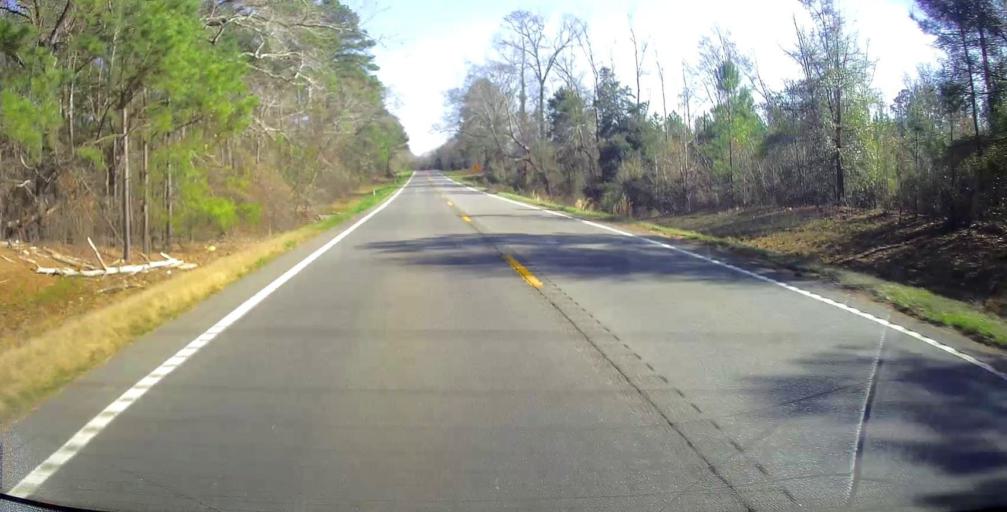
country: US
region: Georgia
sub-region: Macon County
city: Oglethorpe
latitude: 32.3414
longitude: -84.1322
